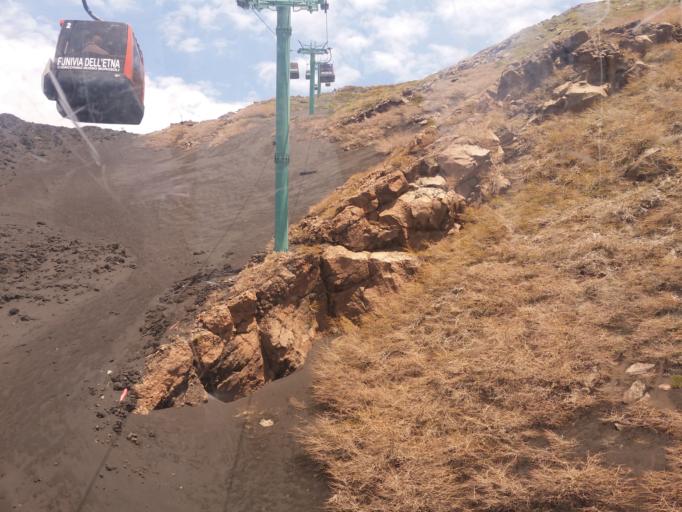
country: IT
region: Sicily
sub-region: Catania
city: Ragalna
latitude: 37.7115
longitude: 14.9996
